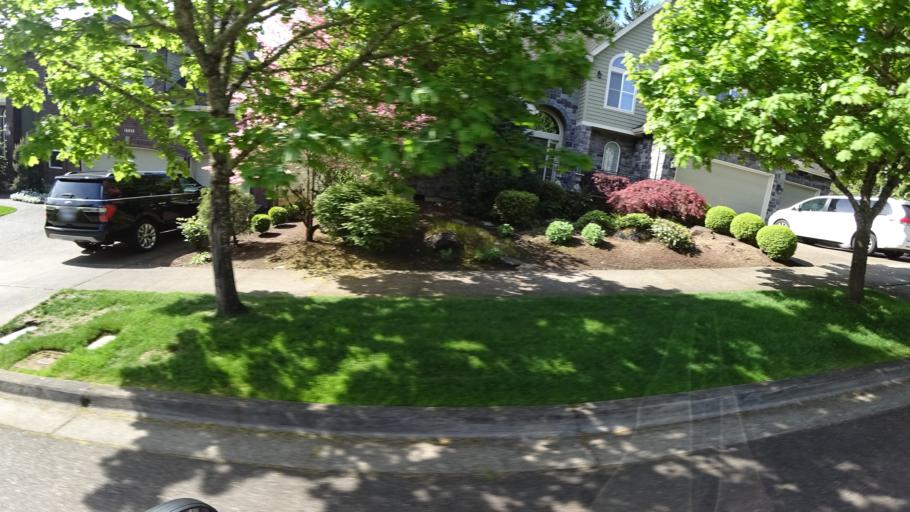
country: US
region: Oregon
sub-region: Washington County
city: Aloha
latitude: 45.4487
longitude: -122.8488
